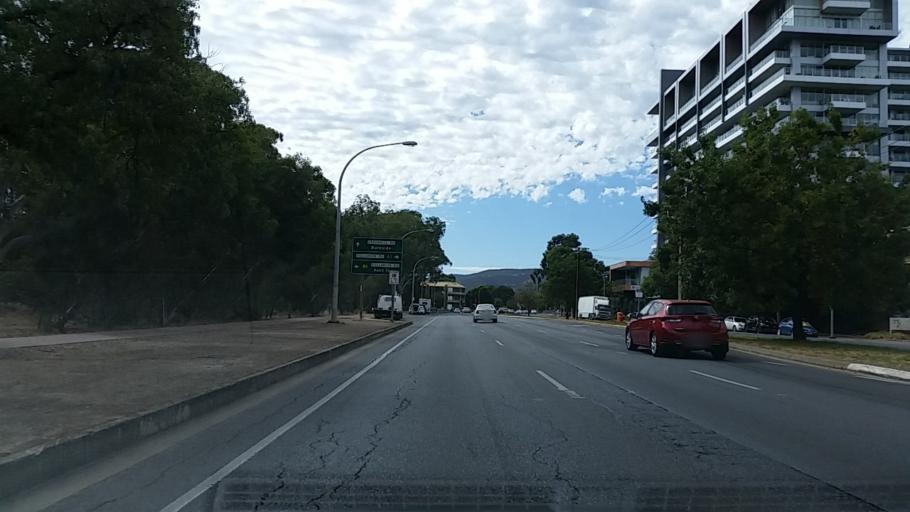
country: AU
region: South Australia
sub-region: Unley
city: Fullarton
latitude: -34.9401
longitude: 138.6214
